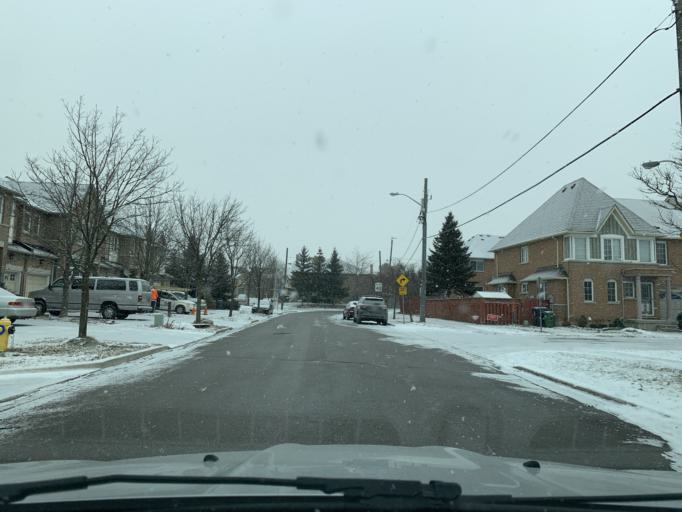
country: CA
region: Ontario
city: Concord
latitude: 43.7427
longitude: -79.4900
